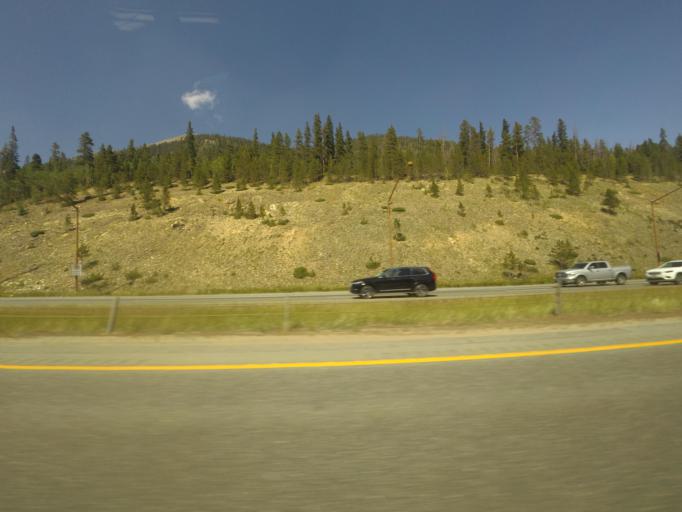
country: US
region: Colorado
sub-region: Clear Creek County
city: Georgetown
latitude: 39.6938
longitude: -105.8207
